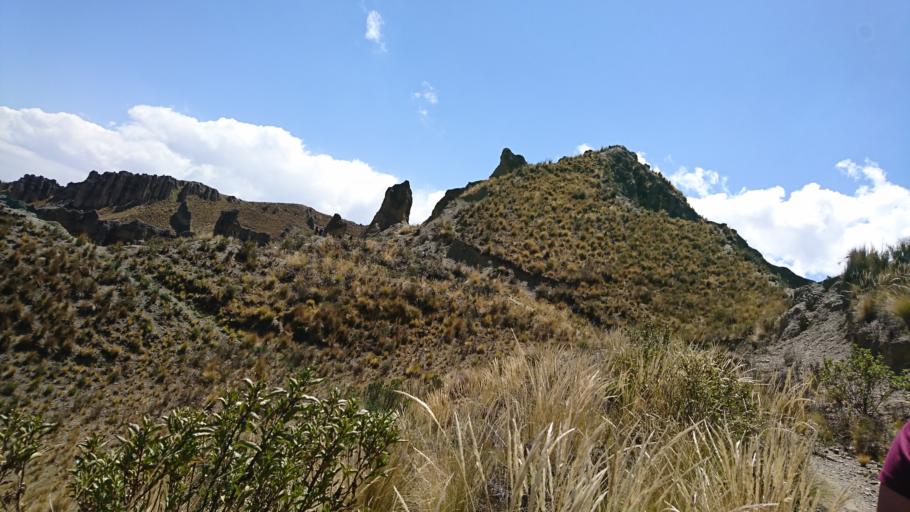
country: BO
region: La Paz
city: La Paz
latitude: -16.5405
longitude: -68.0114
